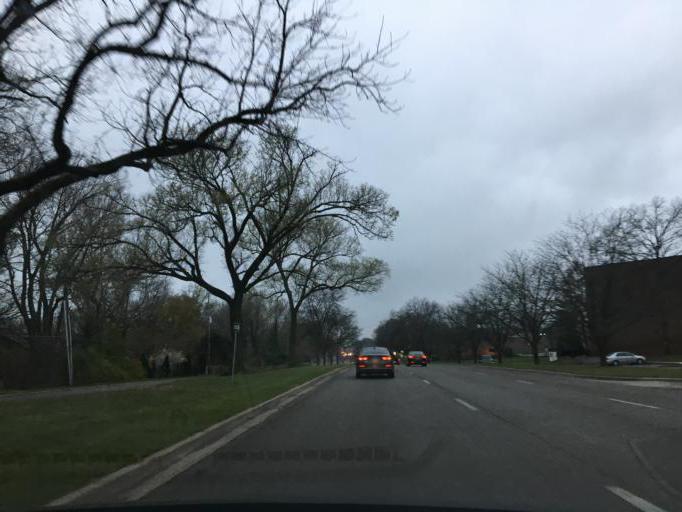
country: US
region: Kansas
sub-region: Johnson County
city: Fairway
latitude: 39.0287
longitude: -94.6338
